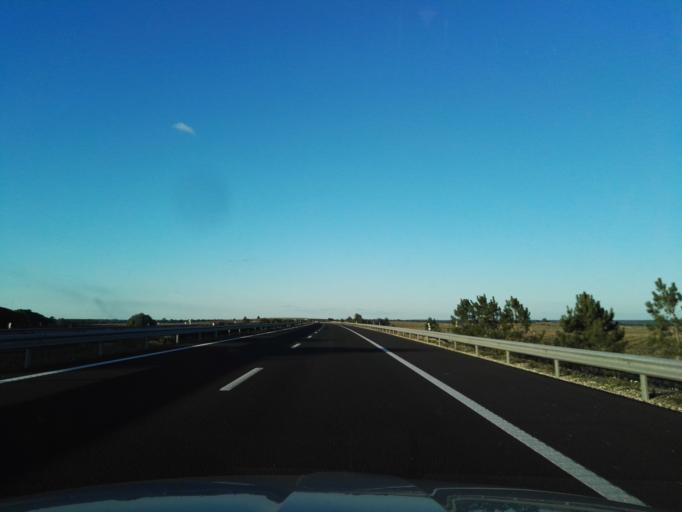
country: PT
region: Santarem
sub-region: Benavente
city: Poceirao
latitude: 38.7676
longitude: -8.6829
